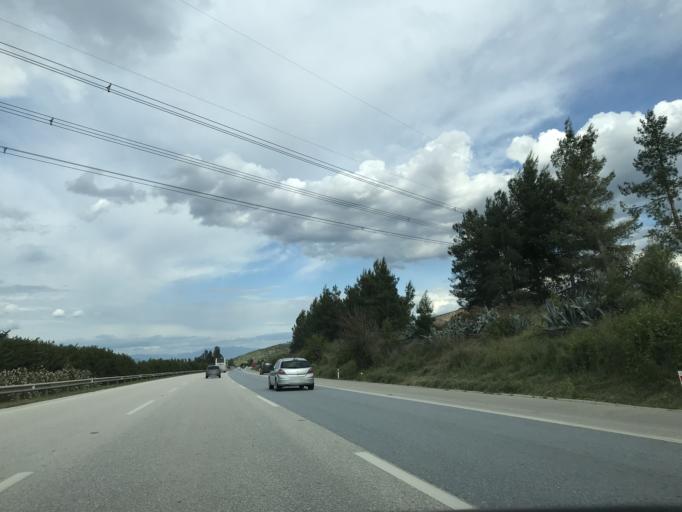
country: TR
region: Adana
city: Yakapinar
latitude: 37.0043
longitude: 35.7137
